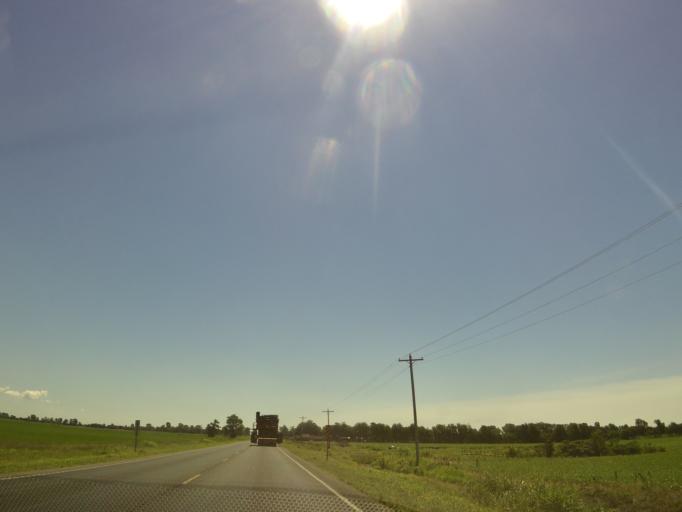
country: US
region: Missouri
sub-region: New Madrid County
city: Portageville
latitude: 36.5538
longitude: -89.7518
